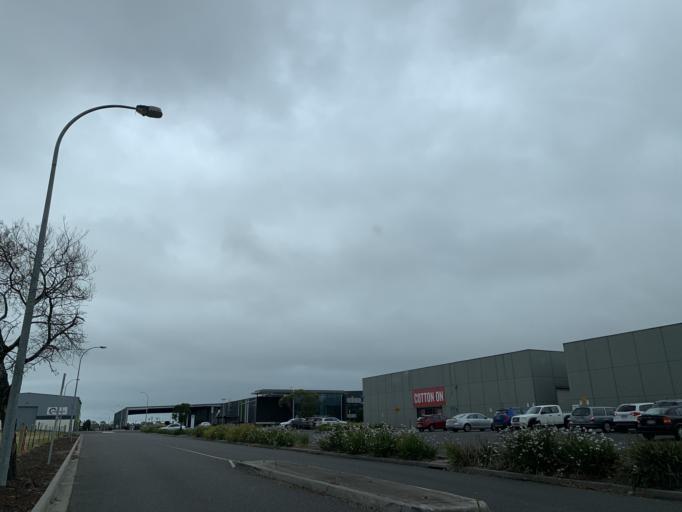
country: AU
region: Victoria
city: Heatherton
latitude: -37.9716
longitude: 145.0900
